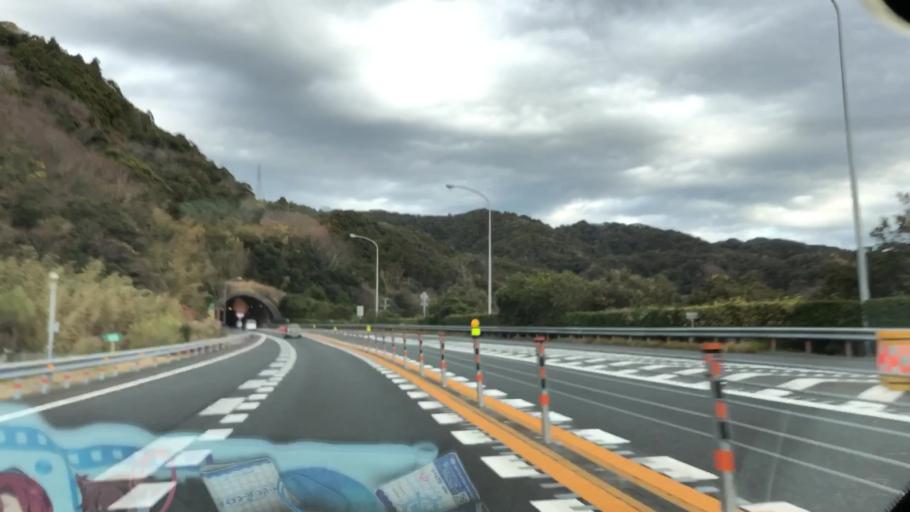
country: JP
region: Chiba
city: Tateyama
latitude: 35.1161
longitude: 139.8515
